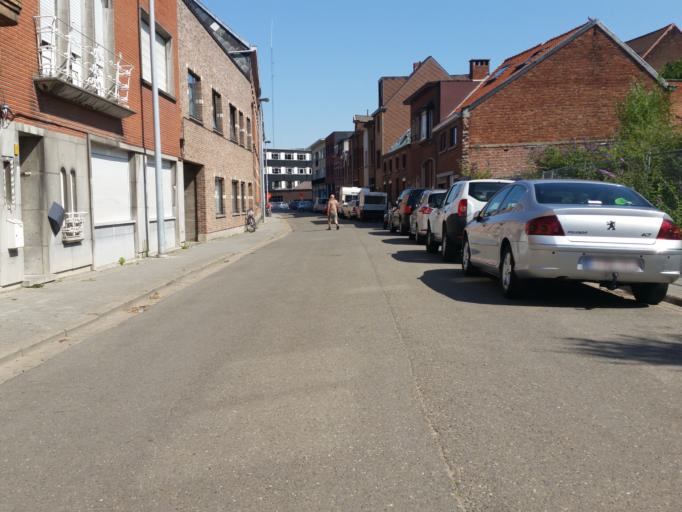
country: BE
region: Flanders
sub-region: Provincie Antwerpen
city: Mechelen
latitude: 51.0257
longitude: 4.4683
